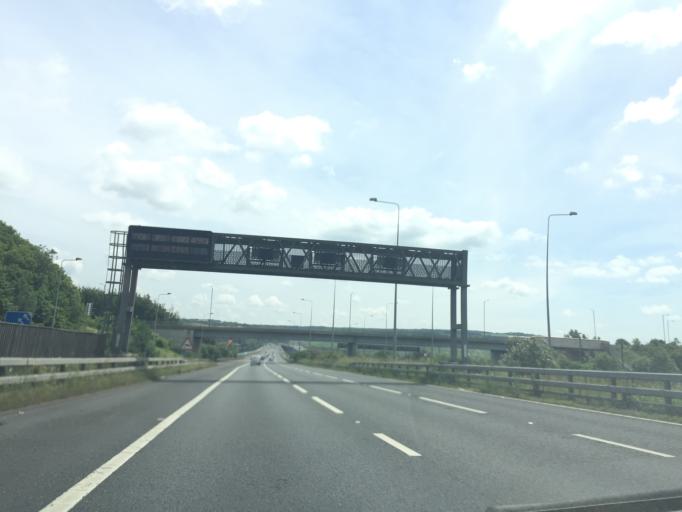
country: GB
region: England
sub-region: Medway
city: Cuxton
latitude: 51.3833
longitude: 0.4689
